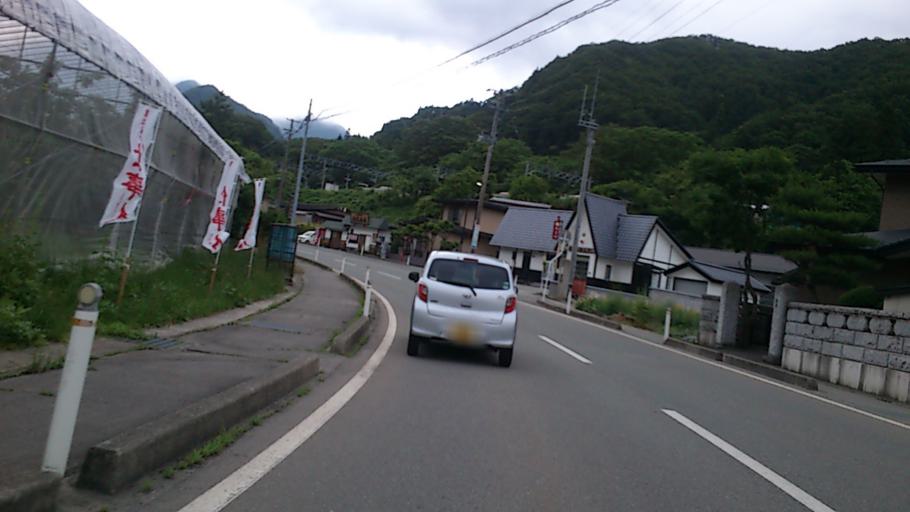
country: JP
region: Yamagata
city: Tendo
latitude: 38.3106
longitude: 140.4315
